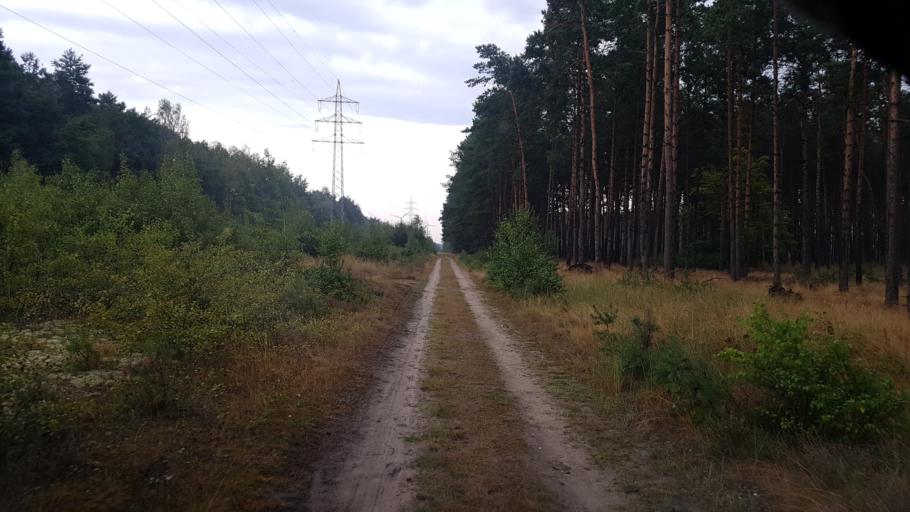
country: DE
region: Brandenburg
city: Finsterwalde
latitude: 51.6389
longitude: 13.7652
